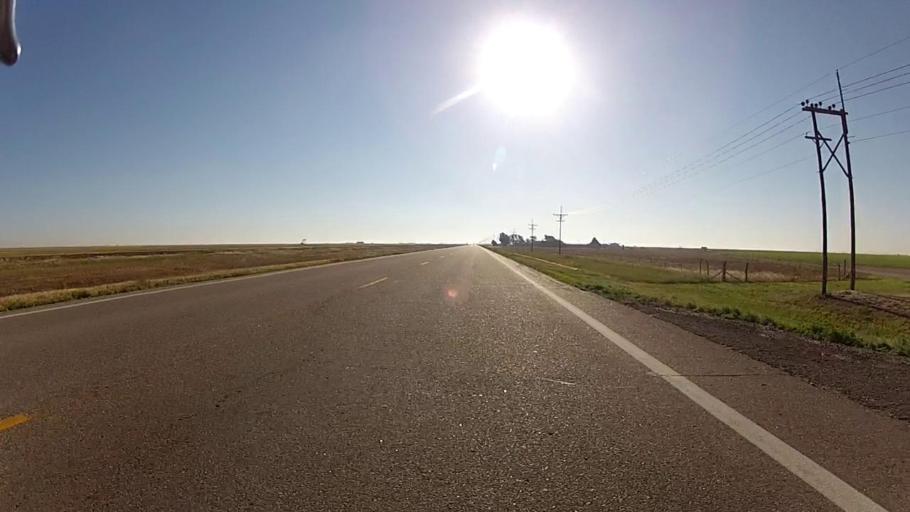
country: US
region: Kansas
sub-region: Haskell County
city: Sublette
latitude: 37.4970
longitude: -100.7953
